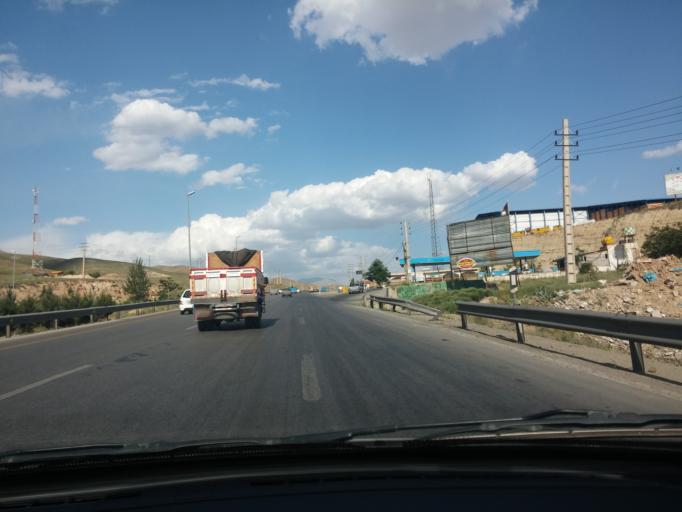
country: IR
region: Tehran
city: Damavand
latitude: 35.7076
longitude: 51.9759
